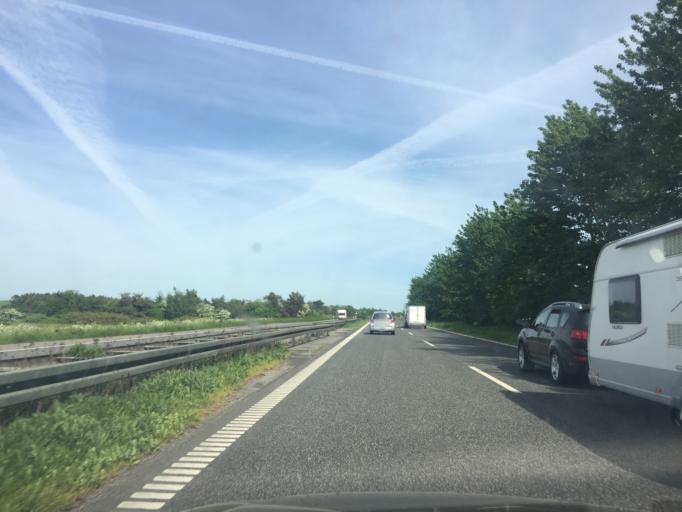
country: DK
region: Zealand
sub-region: Slagelse Kommune
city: Korsor
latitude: 55.3617
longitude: 11.1793
